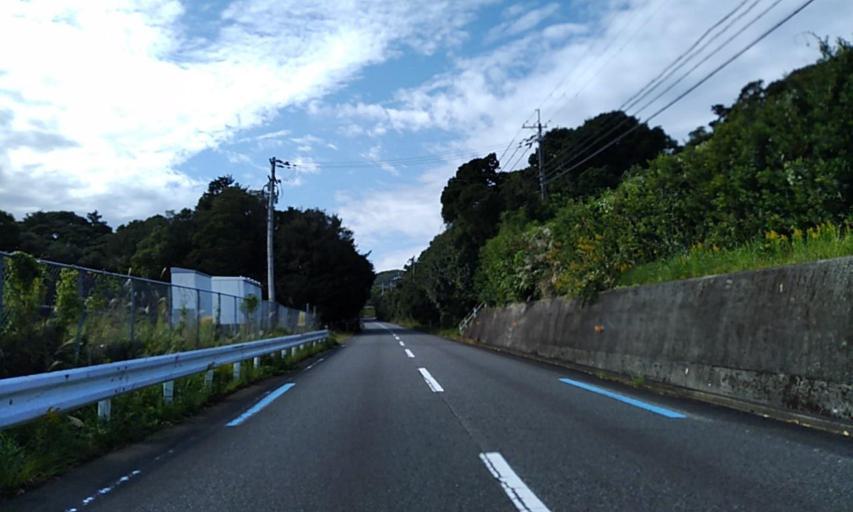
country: JP
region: Wakayama
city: Shingu
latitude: 33.4697
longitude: 135.8421
